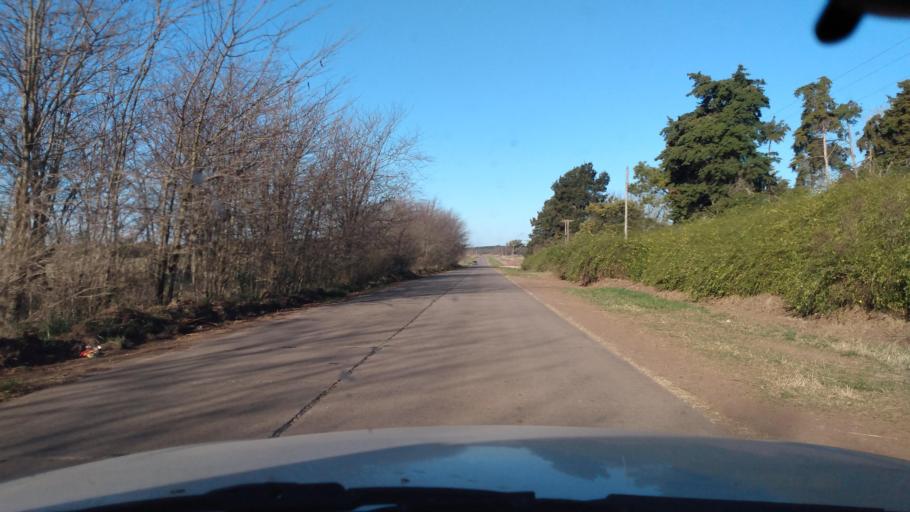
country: AR
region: Buenos Aires
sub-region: Partido de Mercedes
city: Mercedes
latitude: -34.6135
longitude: -59.2762
